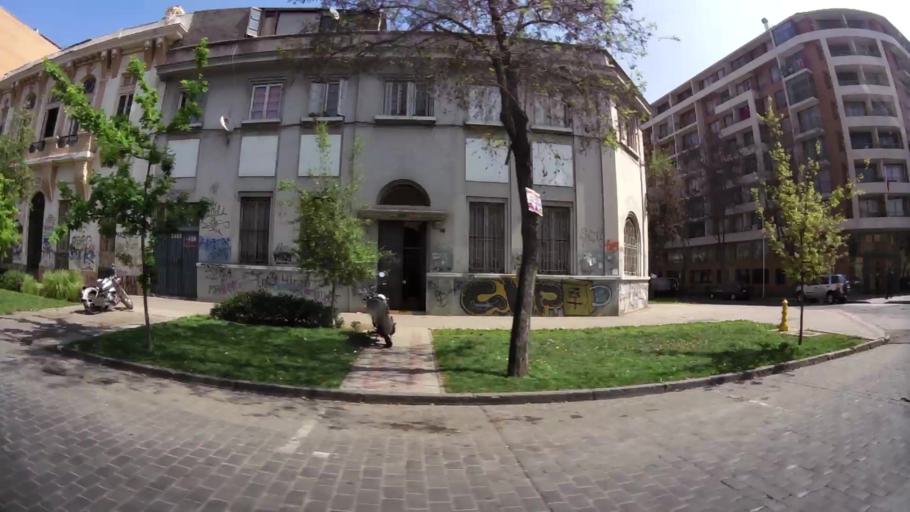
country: CL
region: Santiago Metropolitan
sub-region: Provincia de Santiago
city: Santiago
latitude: -33.4541
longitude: -70.6693
